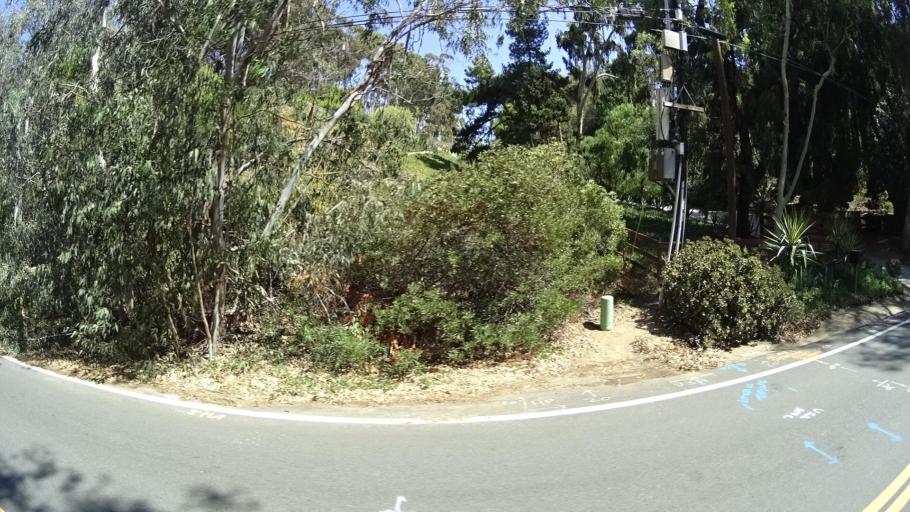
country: US
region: California
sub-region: San Diego County
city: Fairbanks Ranch
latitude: 32.9886
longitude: -117.2246
